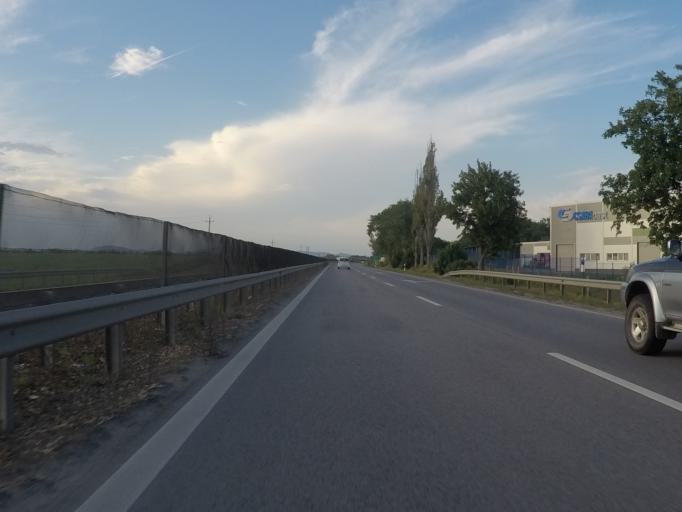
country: HU
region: Heves
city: Zagyvaszanto
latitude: 47.7874
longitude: 19.6618
